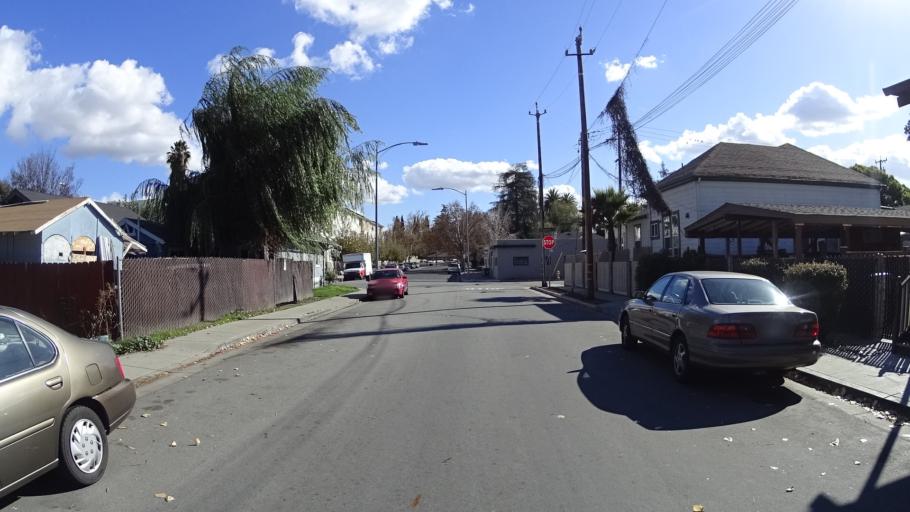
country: US
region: California
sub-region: Santa Clara County
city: Buena Vista
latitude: 37.3347
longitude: -121.9097
